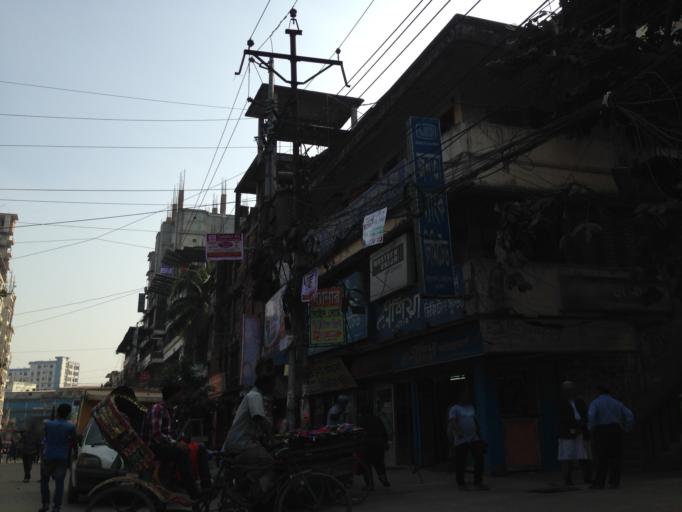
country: BD
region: Dhaka
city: Azimpur
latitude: 23.7995
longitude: 90.3511
